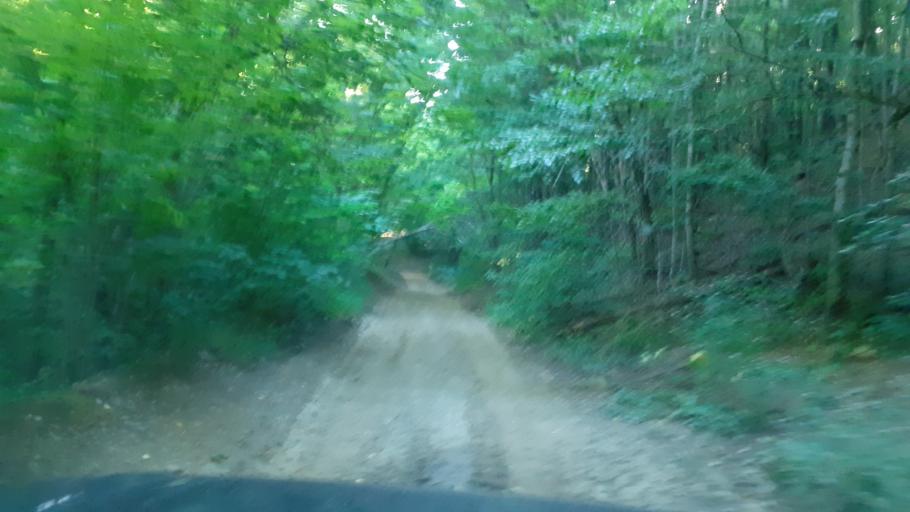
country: RU
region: Krasnodarskiy
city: Pshada
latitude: 44.6573
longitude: 38.4486
